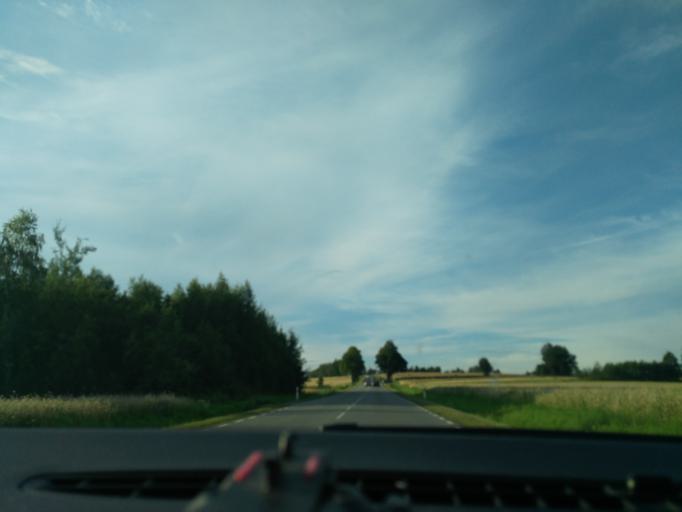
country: PL
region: Lublin Voivodeship
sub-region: Powiat janowski
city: Modliborzyce
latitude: 50.8016
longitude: 22.3193
